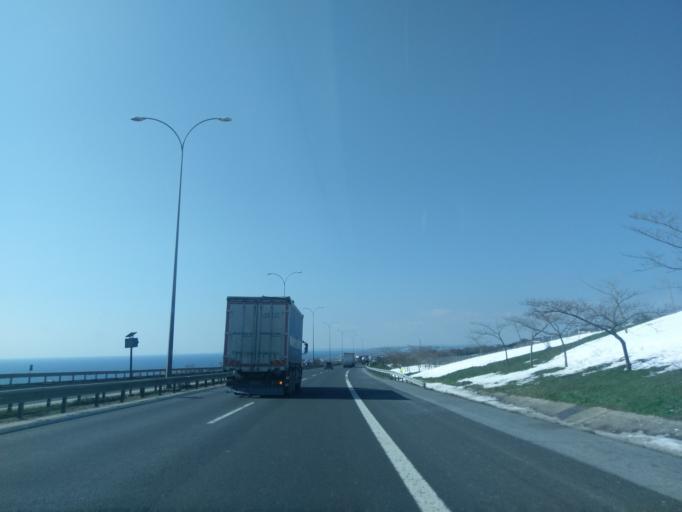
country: TR
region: Istanbul
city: Celaliye
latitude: 41.0507
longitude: 28.4418
